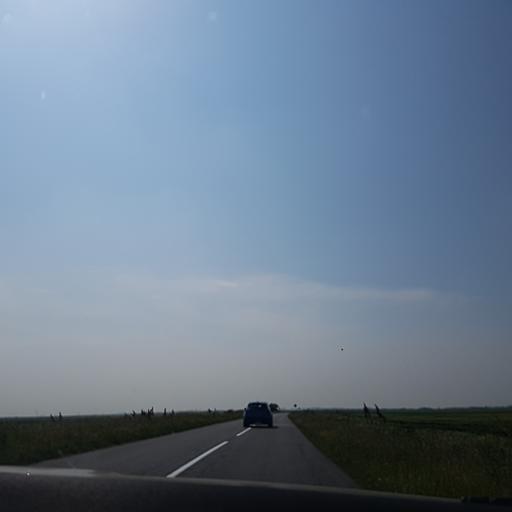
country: RS
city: Jarkovac
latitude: 45.3078
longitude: 20.7559
